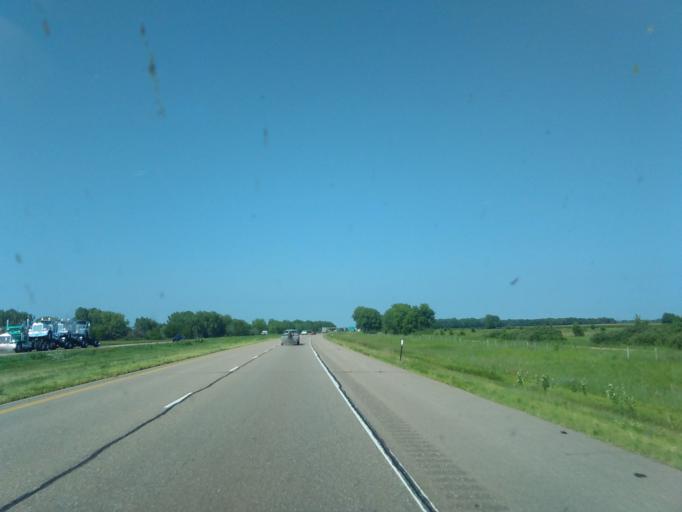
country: US
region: Nebraska
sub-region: Hall County
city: Wood River
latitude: 40.7507
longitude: -98.6162
